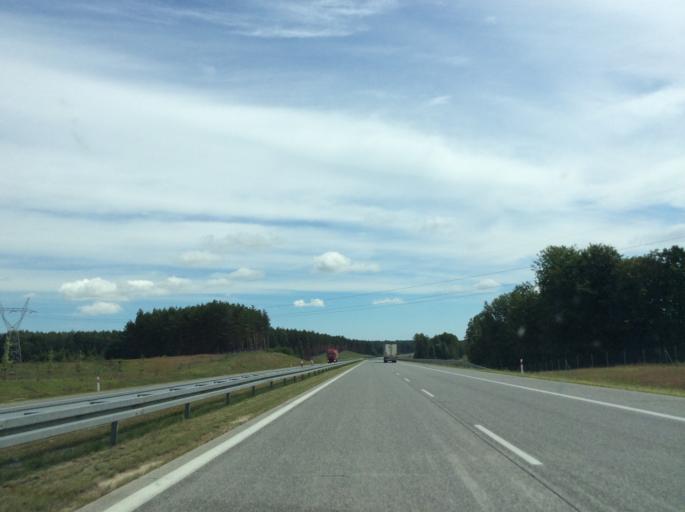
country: PL
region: Lubusz
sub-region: Powiat swiebodzinski
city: Sieniawa
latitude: 52.3148
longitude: 15.3732
